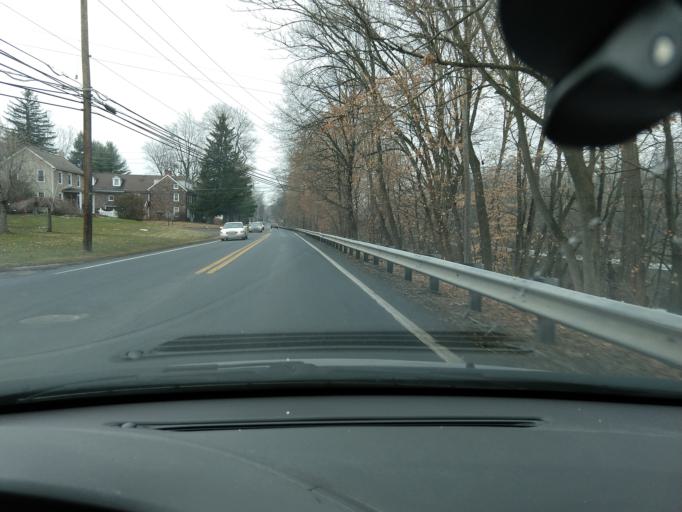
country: US
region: Pennsylvania
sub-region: Berks County
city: Amity Gardens
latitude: 40.2476
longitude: -75.7173
